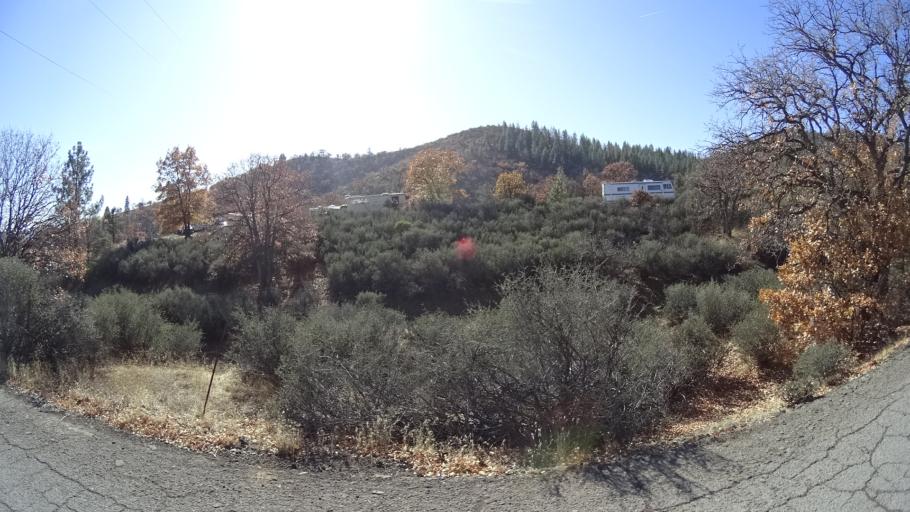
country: US
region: California
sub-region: Siskiyou County
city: Yreka
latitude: 41.7708
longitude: -122.6402
